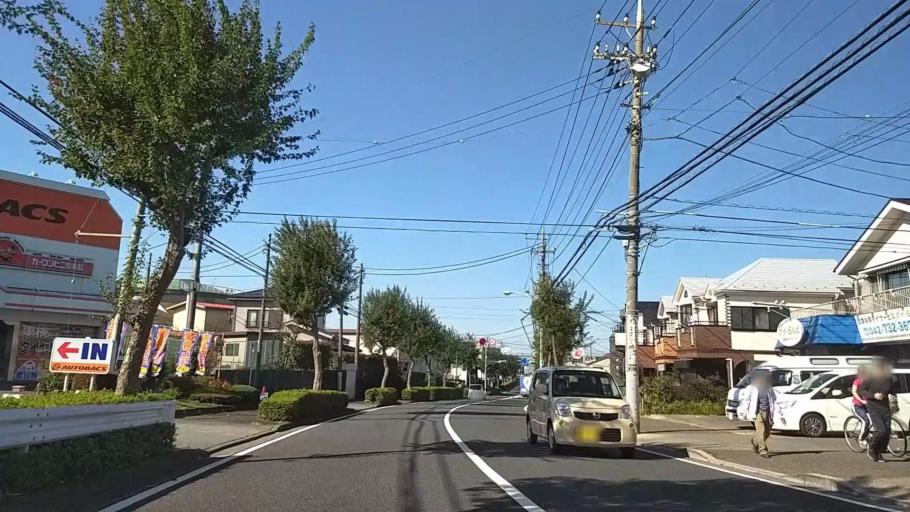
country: JP
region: Tokyo
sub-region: Machida-shi
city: Machida
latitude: 35.5574
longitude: 139.4358
